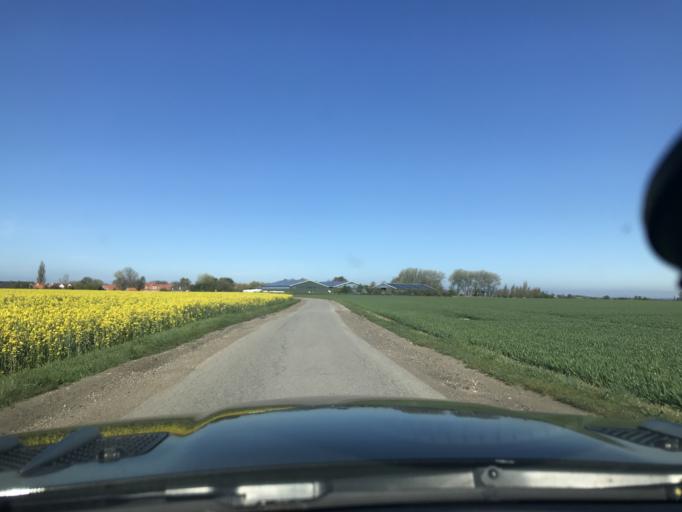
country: DE
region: Schleswig-Holstein
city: Grossenbrode
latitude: 54.4580
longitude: 11.0751
